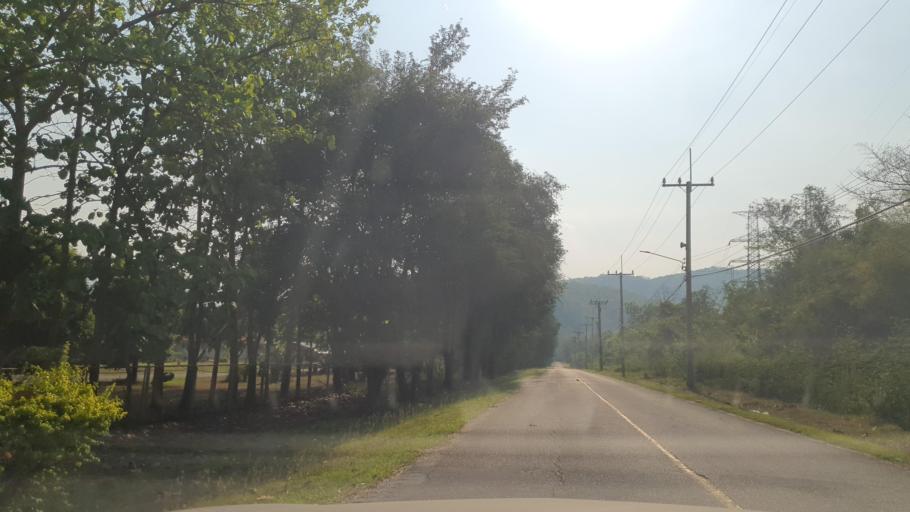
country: TH
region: Kanchanaburi
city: Sai Yok
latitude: 14.2256
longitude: 99.2291
